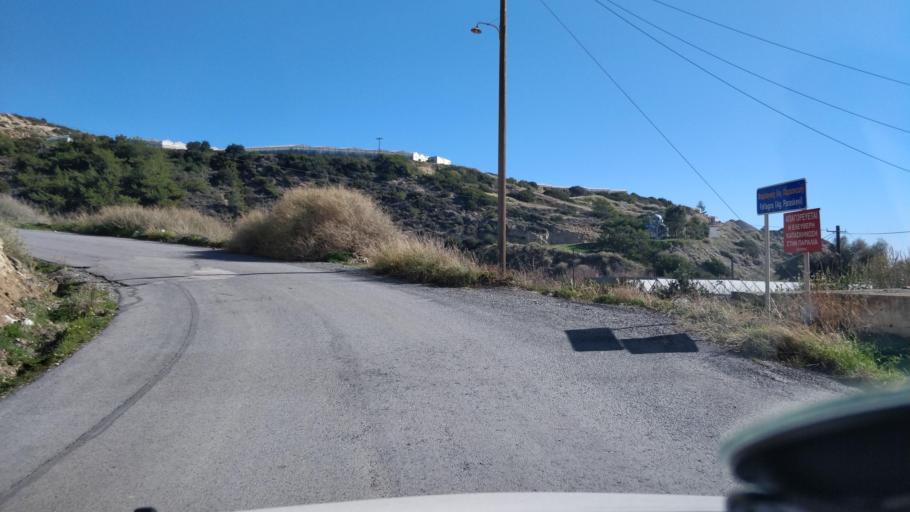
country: GR
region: Crete
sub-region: Nomos Lasithiou
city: Gra Liyia
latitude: 34.9870
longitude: 25.4812
